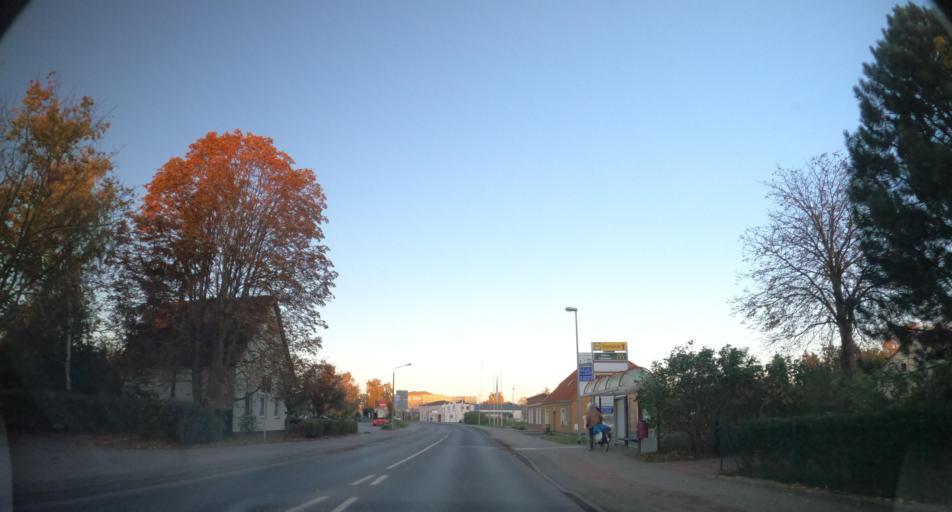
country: DE
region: Mecklenburg-Vorpommern
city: Ueckermunde
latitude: 53.7337
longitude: 14.0366
